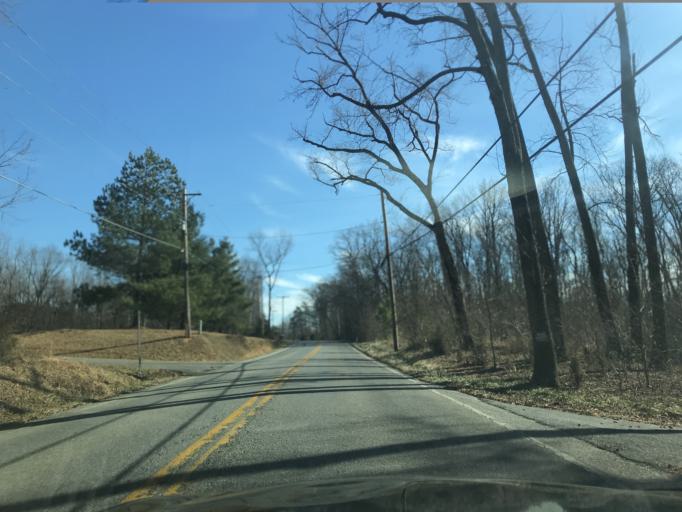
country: US
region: Maryland
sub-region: Charles County
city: Bennsville
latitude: 38.5834
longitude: -77.0423
